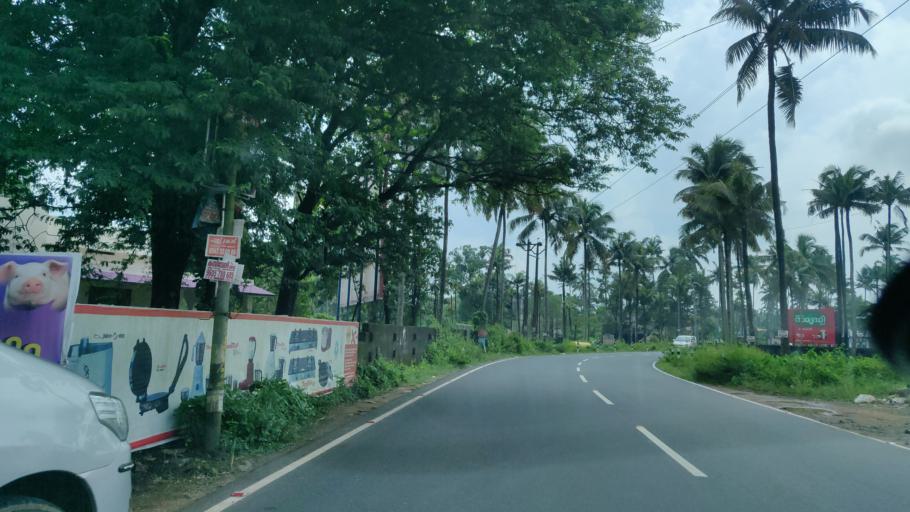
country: IN
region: Kerala
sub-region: Ernakulam
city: Angamali
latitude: 10.1671
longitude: 76.4150
